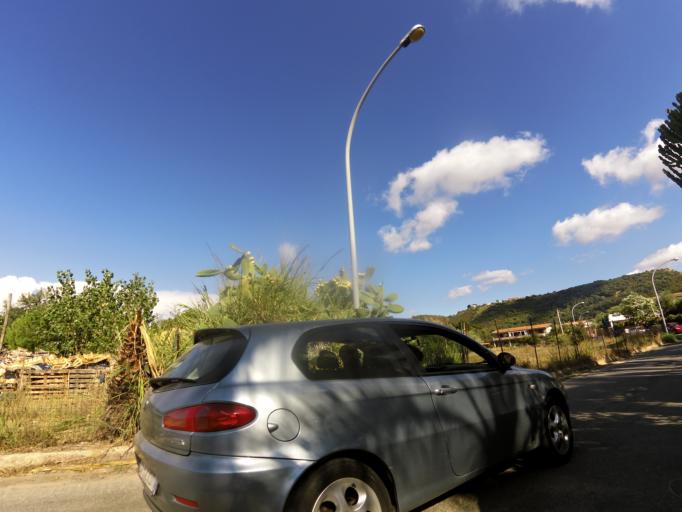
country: IT
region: Calabria
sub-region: Provincia di Vibo-Valentia
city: Santa Domenica
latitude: 38.6693
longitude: 15.8715
